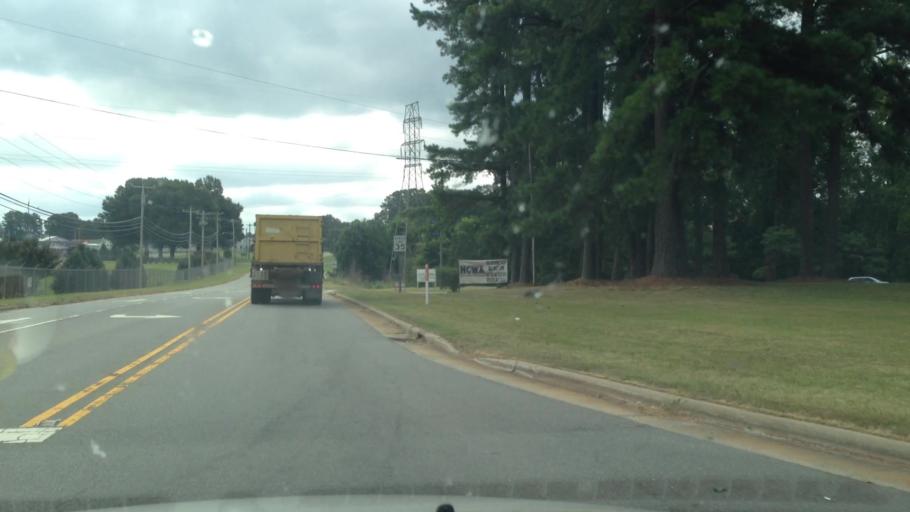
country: US
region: North Carolina
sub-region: Rockingham County
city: Wentworth
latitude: 36.3891
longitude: -79.7501
